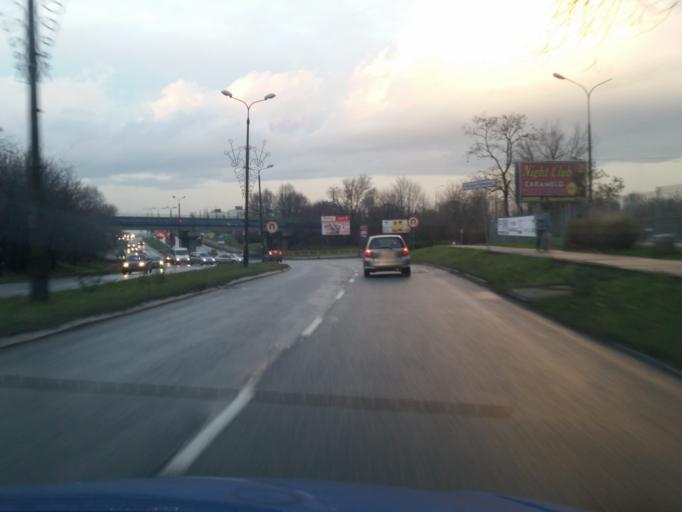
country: PL
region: Silesian Voivodeship
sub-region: Dabrowa Gornicza
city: Dabrowa Gornicza
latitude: 50.3151
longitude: 19.1960
